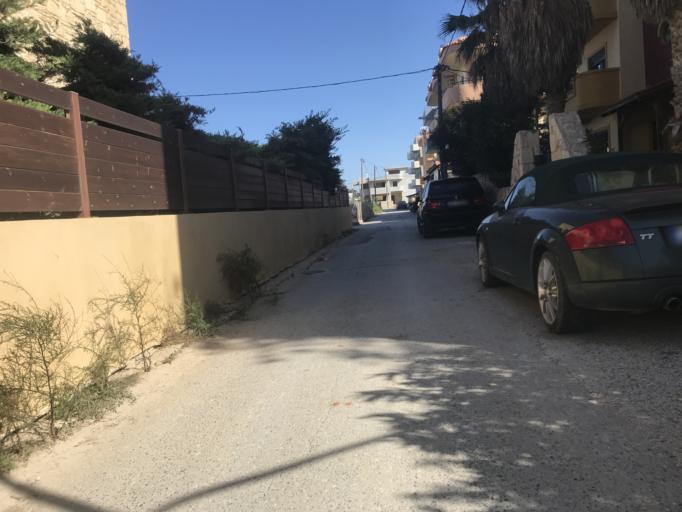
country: GR
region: Crete
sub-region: Nomos Irakleiou
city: Gazi
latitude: 35.3377
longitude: 25.0686
